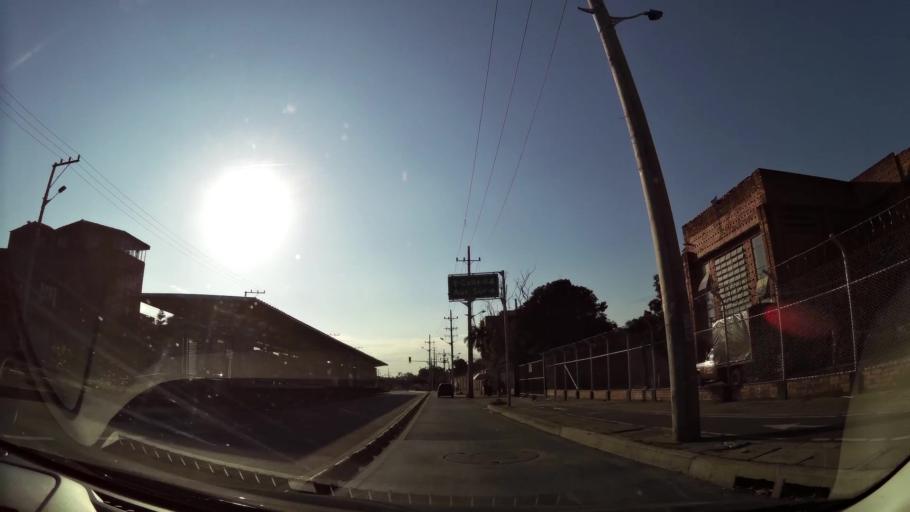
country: CO
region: Valle del Cauca
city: Cali
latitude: 3.4375
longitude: -76.5180
